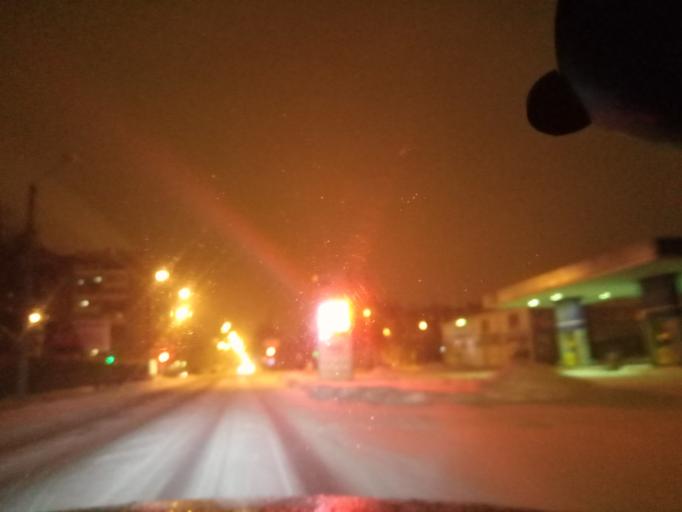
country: RU
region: Tula
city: Novomoskovsk
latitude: 54.0036
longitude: 38.2961
